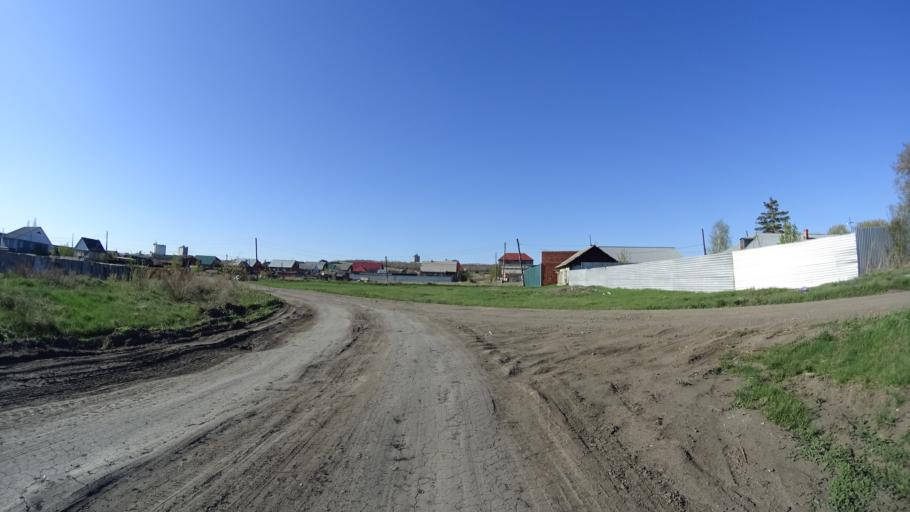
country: RU
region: Chelyabinsk
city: Troitsk
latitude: 54.0954
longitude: 61.5984
